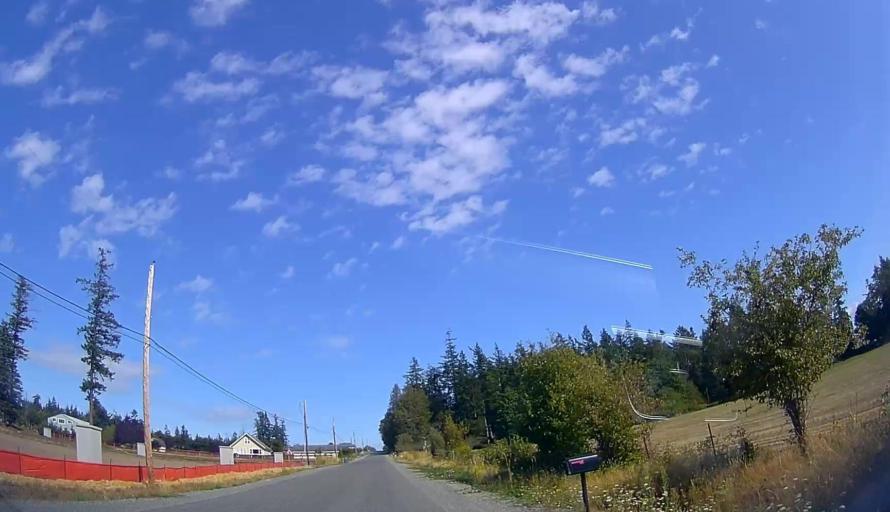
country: US
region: Washington
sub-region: Skagit County
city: Anacortes
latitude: 48.5012
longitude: -122.4787
